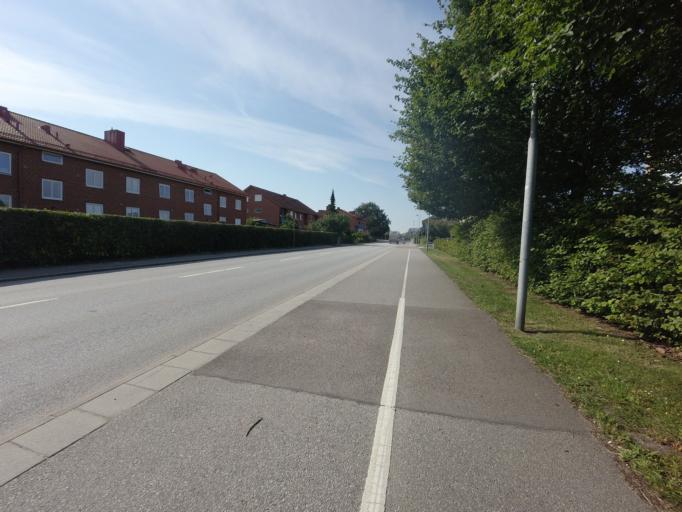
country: SE
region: Skane
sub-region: Vellinge Kommun
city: Vellinge
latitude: 55.4730
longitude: 13.0148
